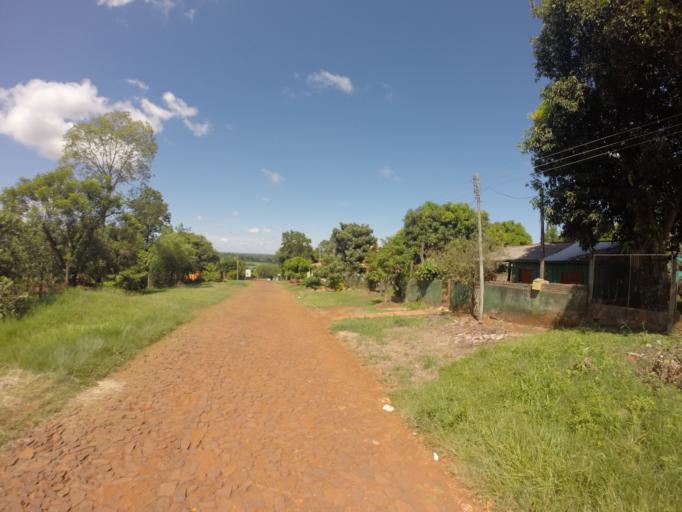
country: PY
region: Alto Parana
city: Ciudad del Este
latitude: -25.4402
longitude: -54.6421
